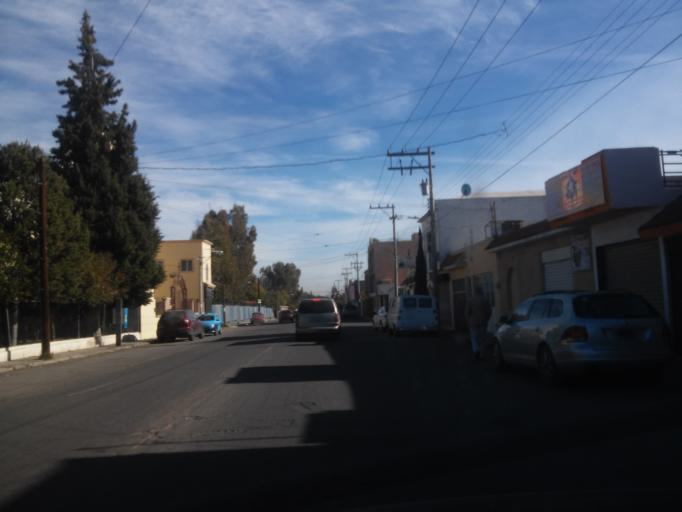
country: MX
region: Durango
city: Victoria de Durango
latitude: 24.0407
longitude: -104.6554
